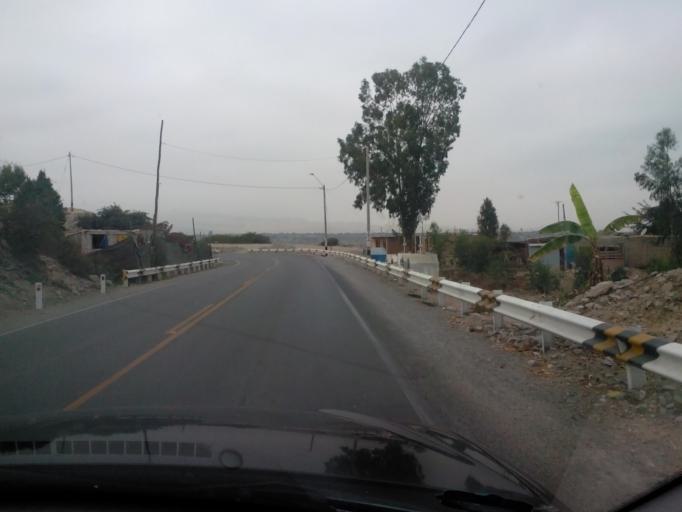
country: PE
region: Ica
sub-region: Provincia de Pisco
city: Humay
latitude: -13.7312
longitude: -75.9364
